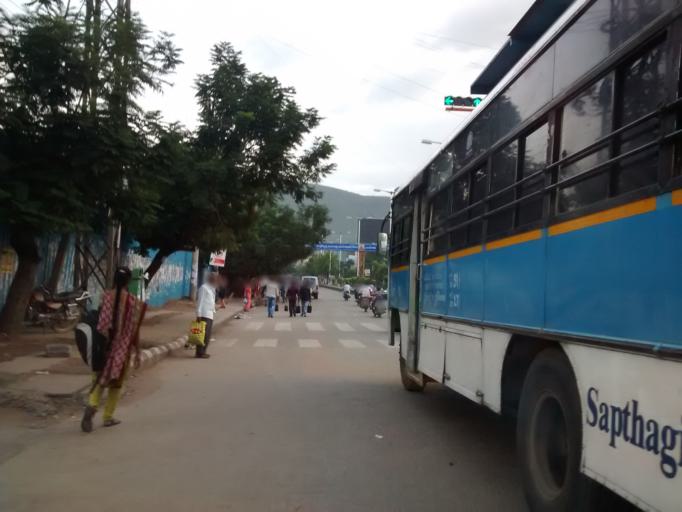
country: IN
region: Andhra Pradesh
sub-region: Chittoor
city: Tirupati
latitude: 13.6418
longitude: 79.4275
